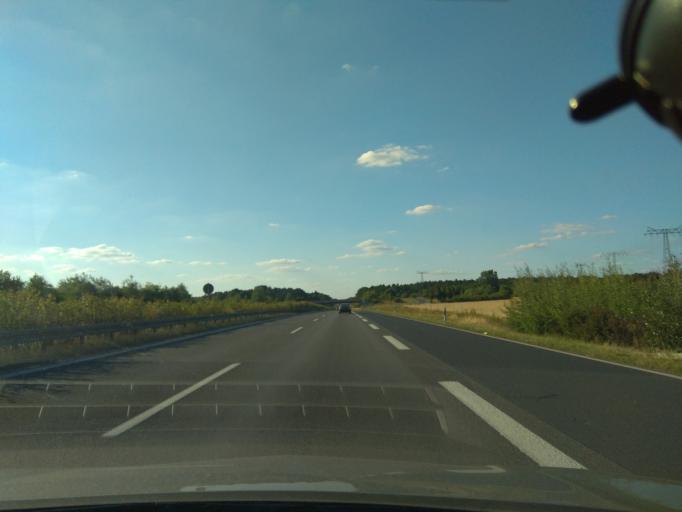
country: DE
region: Brandenburg
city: Mittenwalde
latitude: 52.2621
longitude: 13.5791
